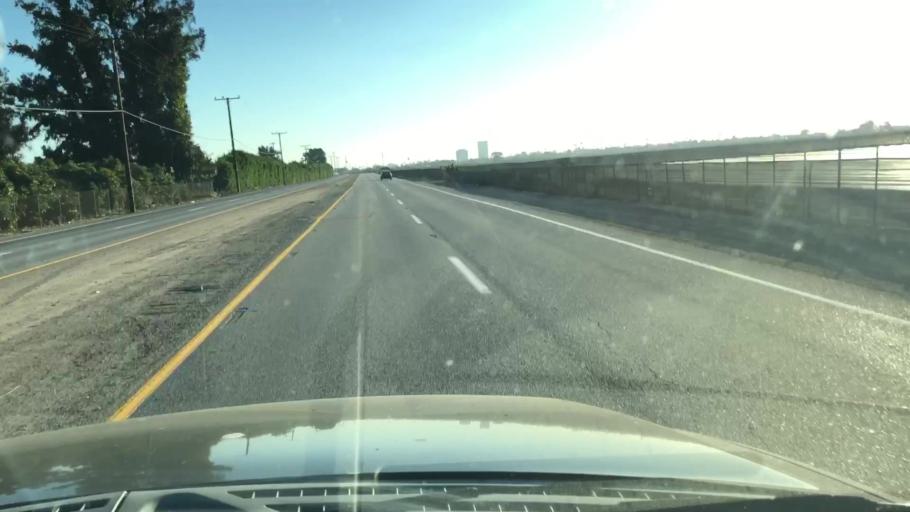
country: US
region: California
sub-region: Ventura County
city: El Rio
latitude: 34.2487
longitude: -119.1450
